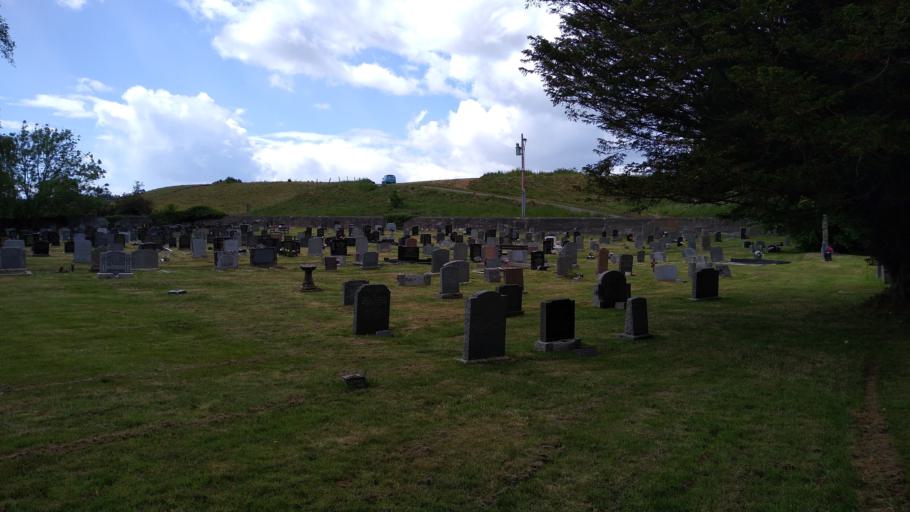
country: GB
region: England
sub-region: Cumbria
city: Flimby
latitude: 54.6559
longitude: -3.4967
